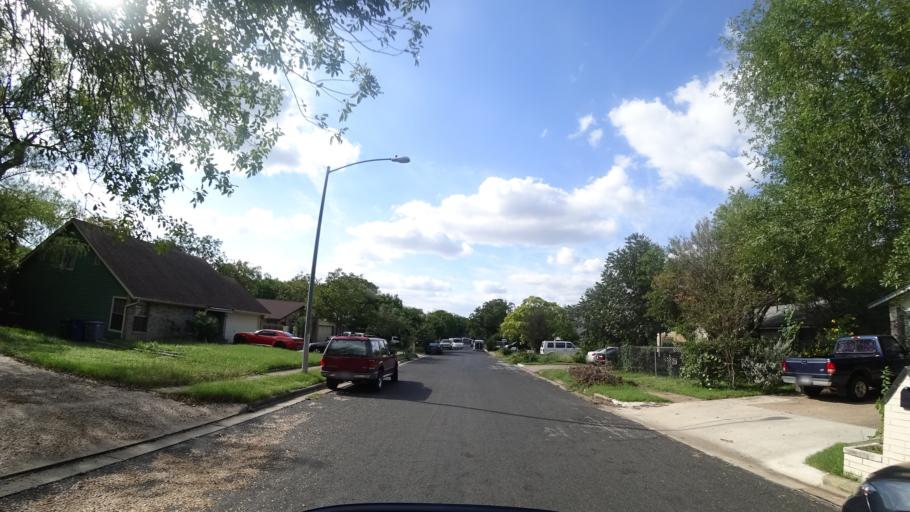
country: US
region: Texas
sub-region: Travis County
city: Rollingwood
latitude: 30.2085
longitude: -97.7938
